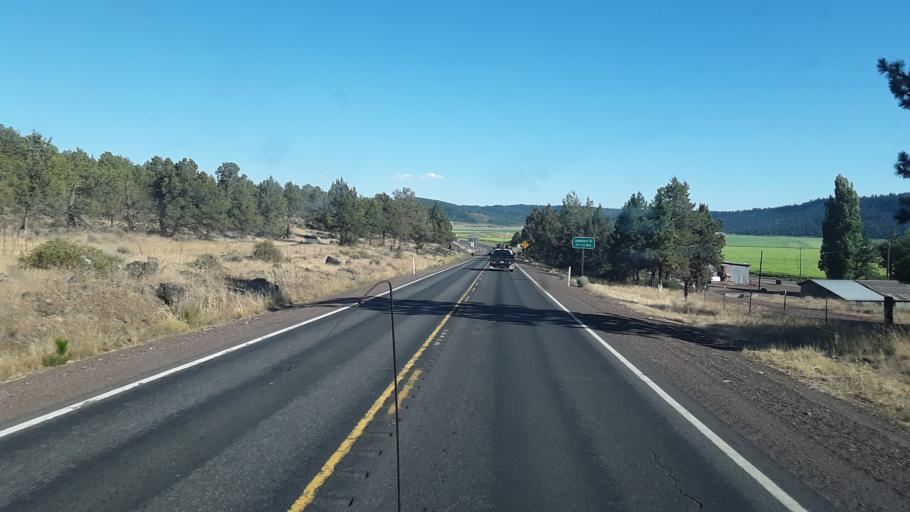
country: US
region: Oregon
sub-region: Klamath County
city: Klamath Falls
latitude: 42.2653
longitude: -121.8779
